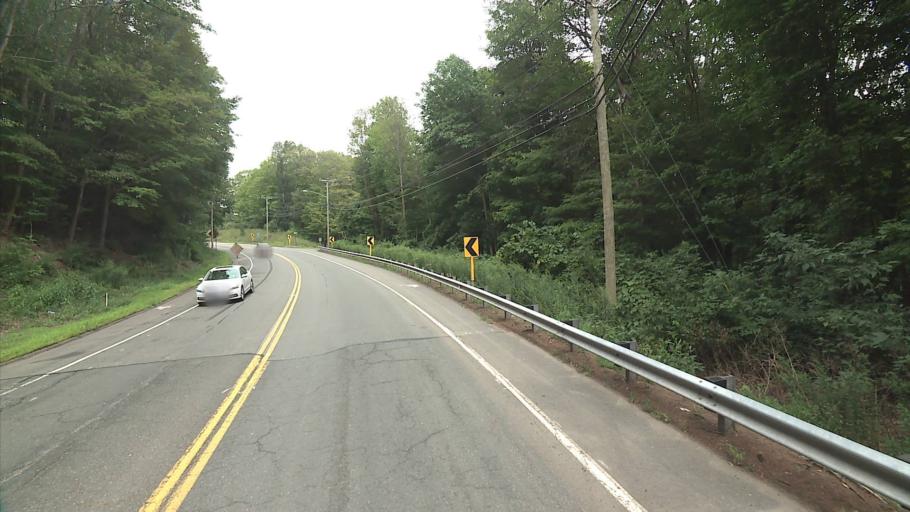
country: US
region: Connecticut
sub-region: Tolland County
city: Tolland
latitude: 41.8835
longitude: -72.3082
